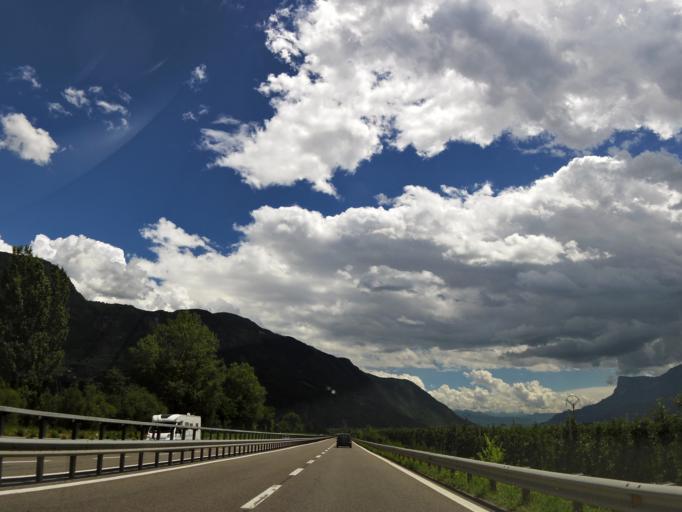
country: IT
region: Trentino-Alto Adige
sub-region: Bolzano
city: Marlengo
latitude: 46.6478
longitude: 11.1573
